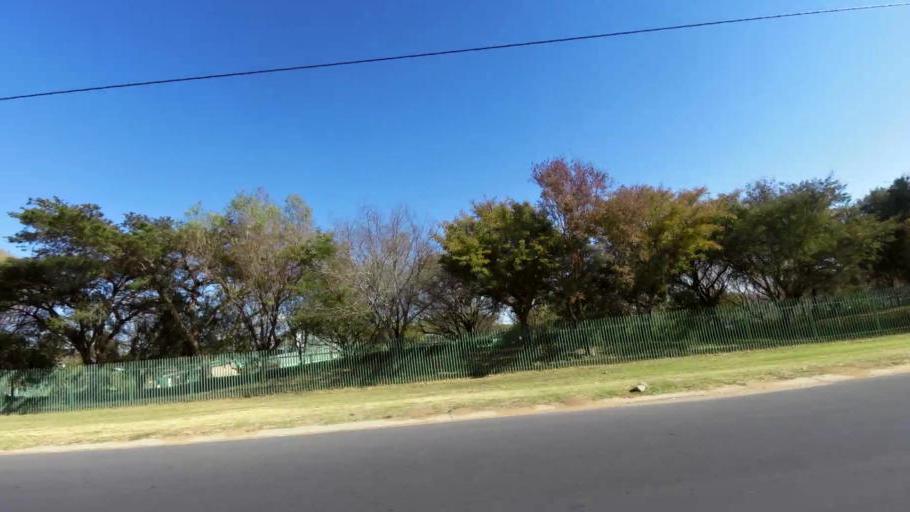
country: ZA
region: Gauteng
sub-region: City of Johannesburg Metropolitan Municipality
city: Johannesburg
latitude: -26.2429
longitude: 27.9982
